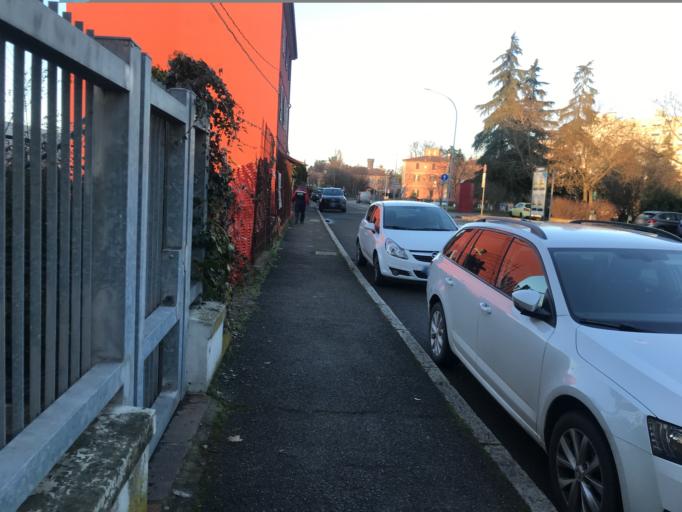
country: IT
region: Emilia-Romagna
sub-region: Provincia di Bologna
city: Progresso
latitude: 44.5408
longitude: 11.3513
